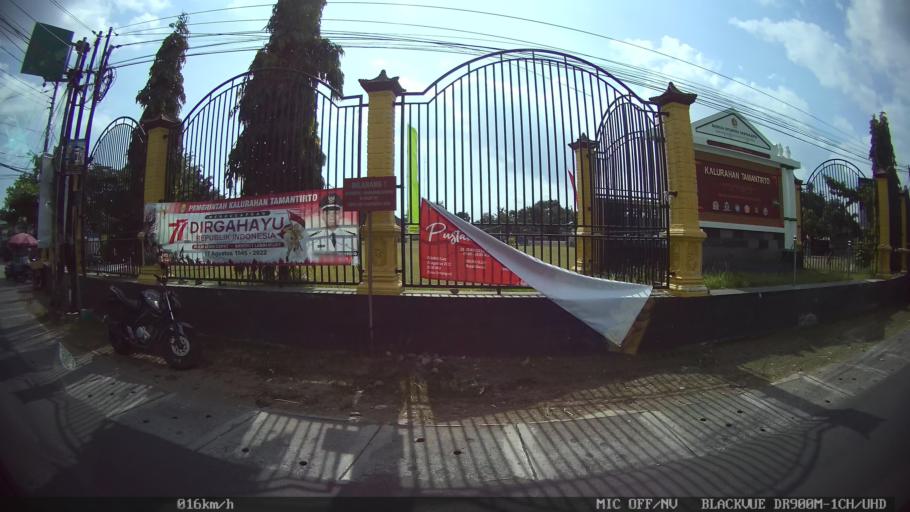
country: ID
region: Daerah Istimewa Yogyakarta
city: Kasihan
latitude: -7.8255
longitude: 110.3281
